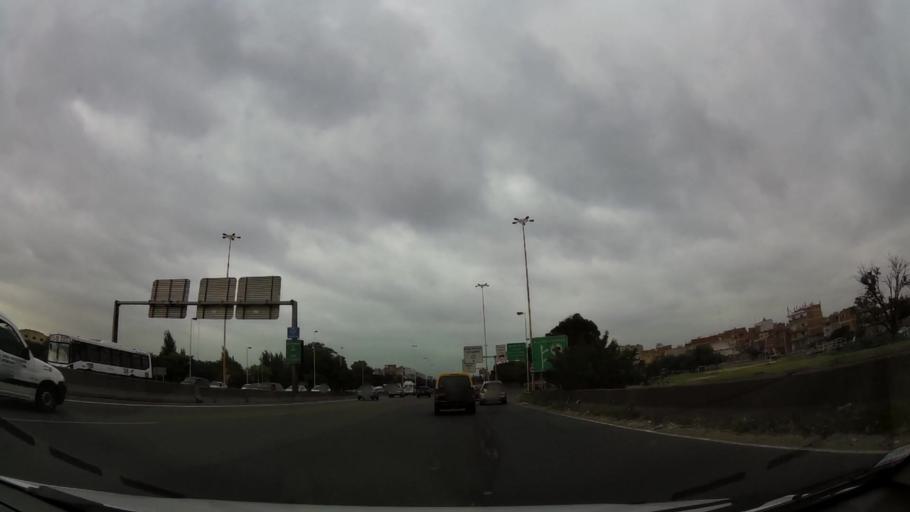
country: AR
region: Buenos Aires F.D.
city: Villa Lugano
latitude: -34.6881
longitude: -58.4865
